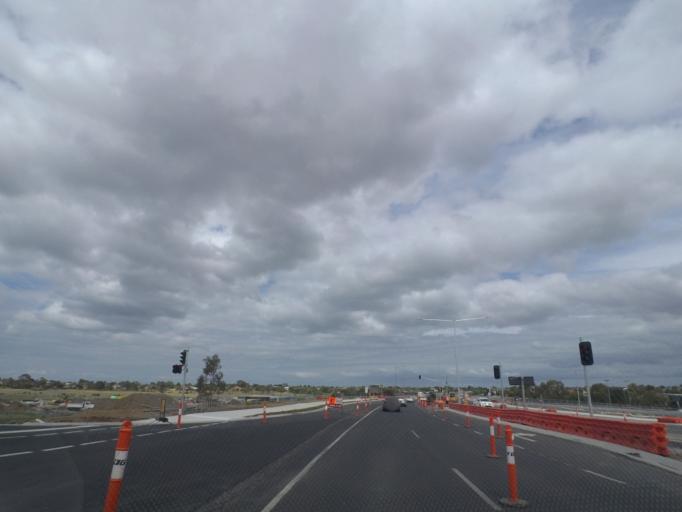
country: AU
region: Victoria
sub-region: Wyndham
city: Williams Landing
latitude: -37.8723
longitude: 144.7489
